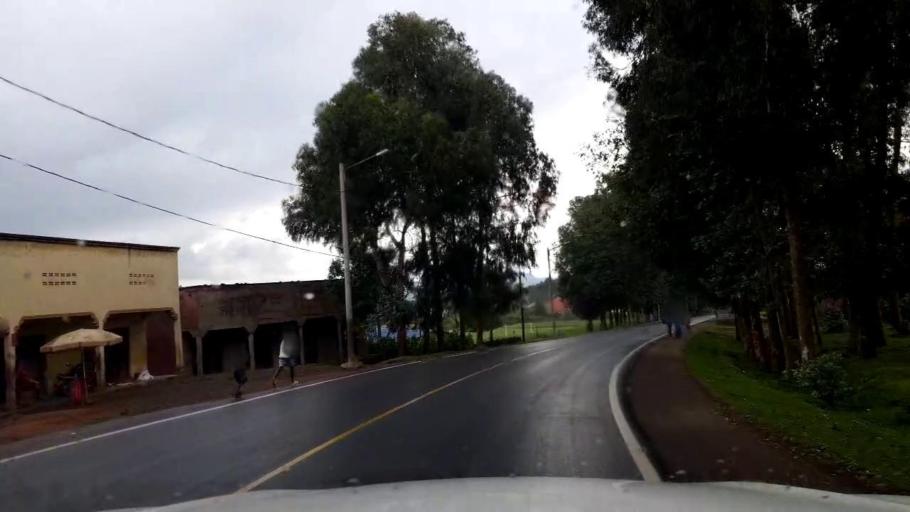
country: RW
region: Western Province
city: Gisenyi
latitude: -1.6773
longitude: 29.3554
